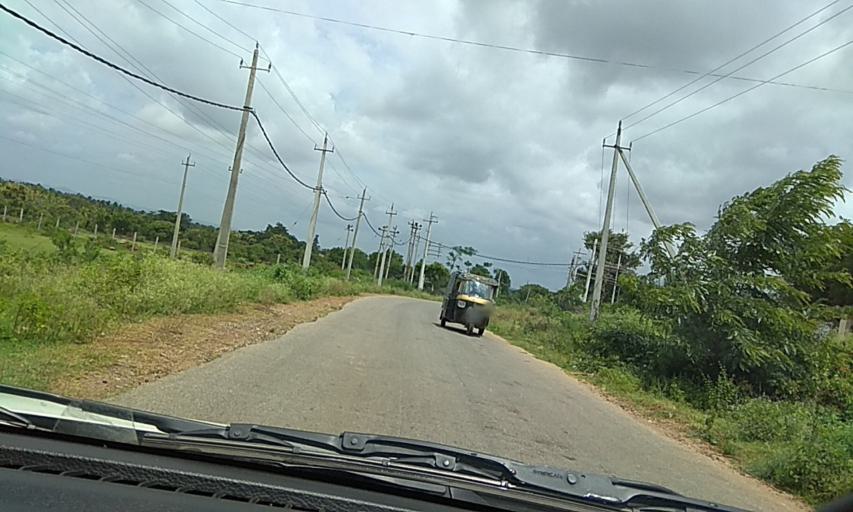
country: IN
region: Karnataka
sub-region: Chamrajnagar
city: Gundlupet
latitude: 11.8008
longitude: 76.7951
